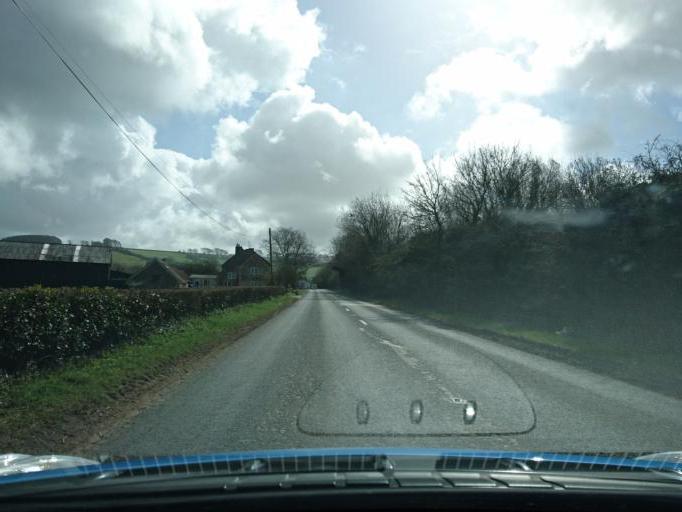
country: GB
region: England
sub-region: South Gloucestershire
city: Pucklechurch
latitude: 51.4519
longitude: -2.4138
